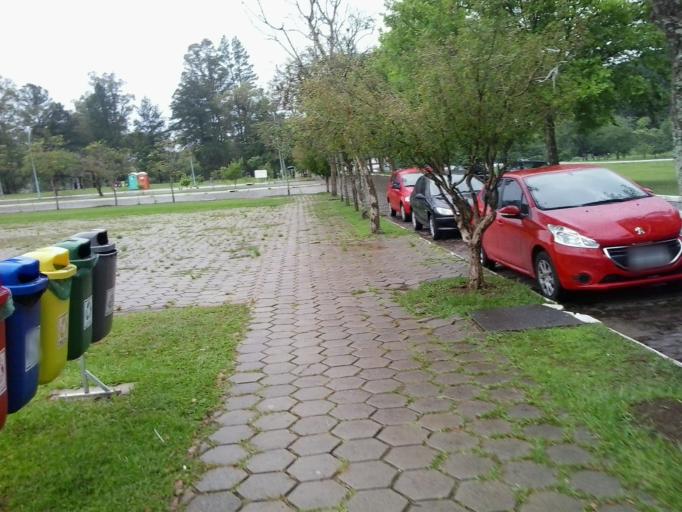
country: BR
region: Rio Grande do Sul
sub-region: Santa Maria
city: Santa Maria
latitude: -29.7207
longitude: -53.7173
